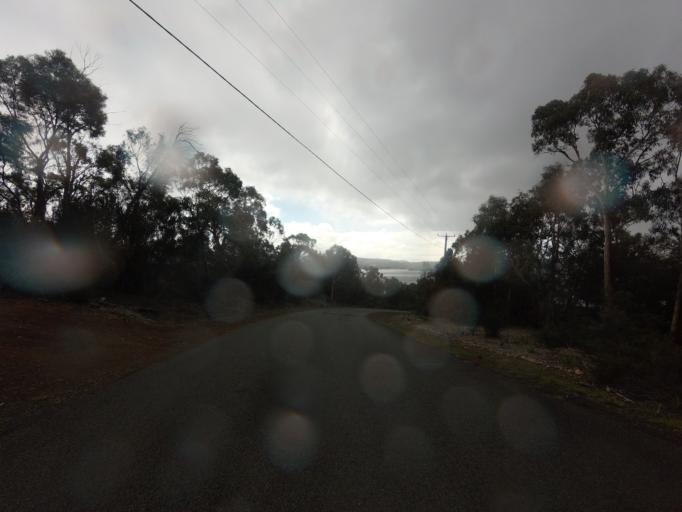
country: AU
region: Tasmania
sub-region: Sorell
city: Sorell
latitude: -42.5334
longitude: 147.9123
